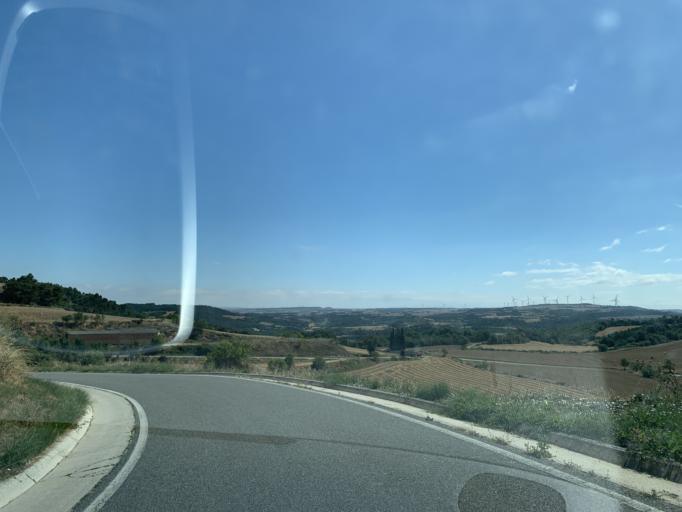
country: ES
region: Catalonia
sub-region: Provincia de Tarragona
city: Conesa
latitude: 41.5429
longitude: 1.3017
